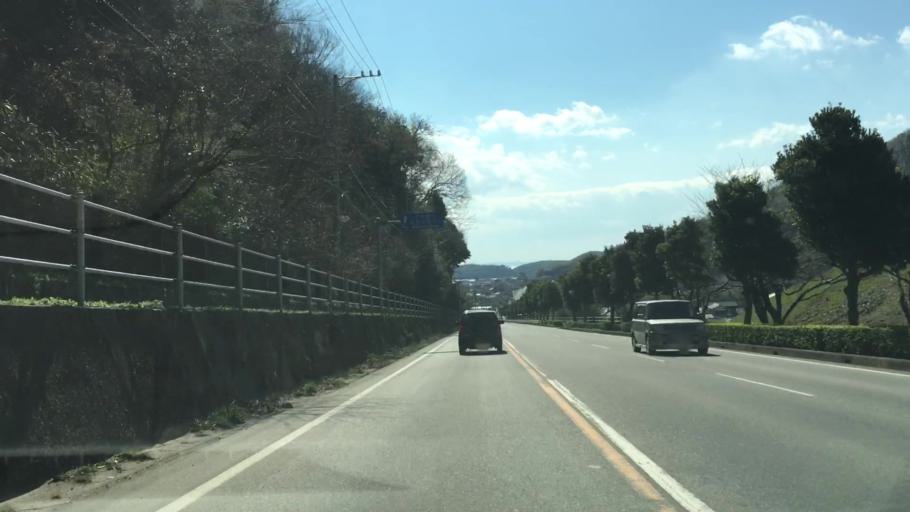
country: JP
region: Aichi
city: Gamagori
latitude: 34.7984
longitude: 137.1627
